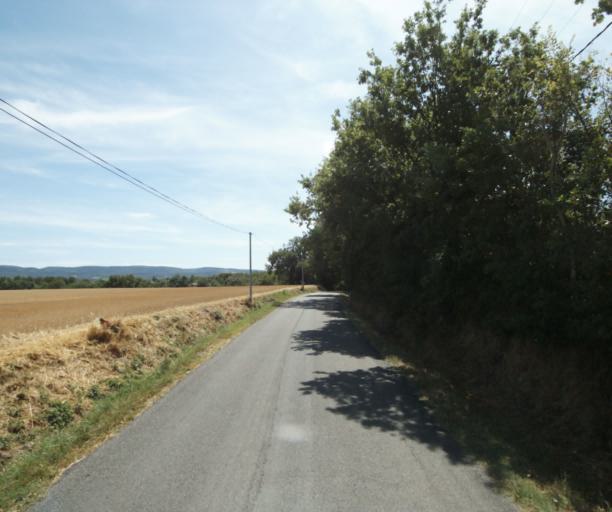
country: FR
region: Midi-Pyrenees
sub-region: Departement de la Haute-Garonne
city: Revel
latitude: 43.4970
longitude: 2.0218
